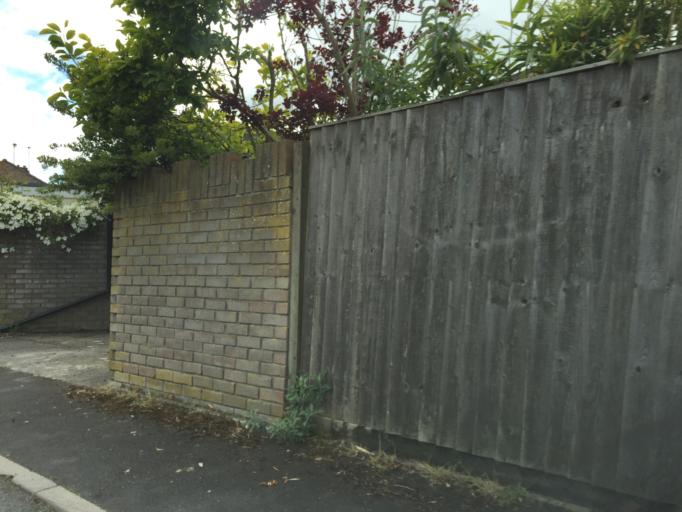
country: GB
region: England
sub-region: South Gloucestershire
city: Thornbury
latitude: 51.6168
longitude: -2.5224
